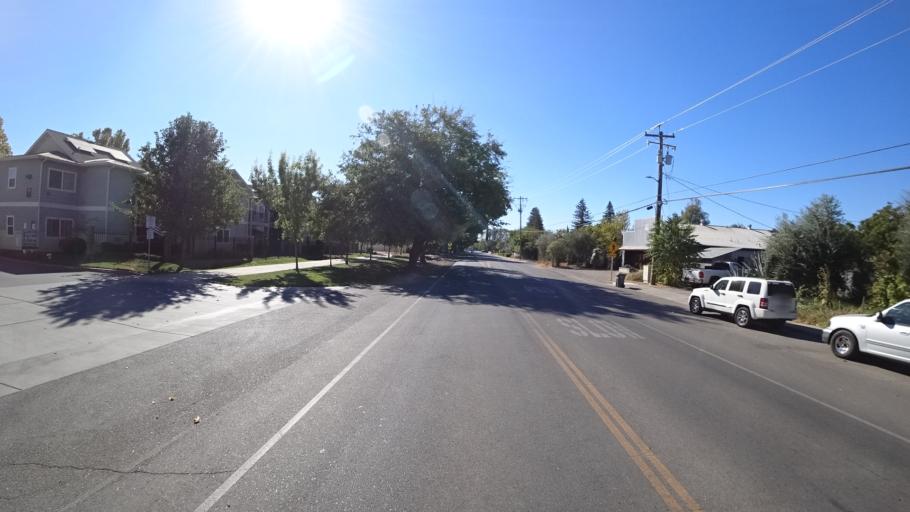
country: US
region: California
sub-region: Yolo County
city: Winters
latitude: 38.5294
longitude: -121.9711
